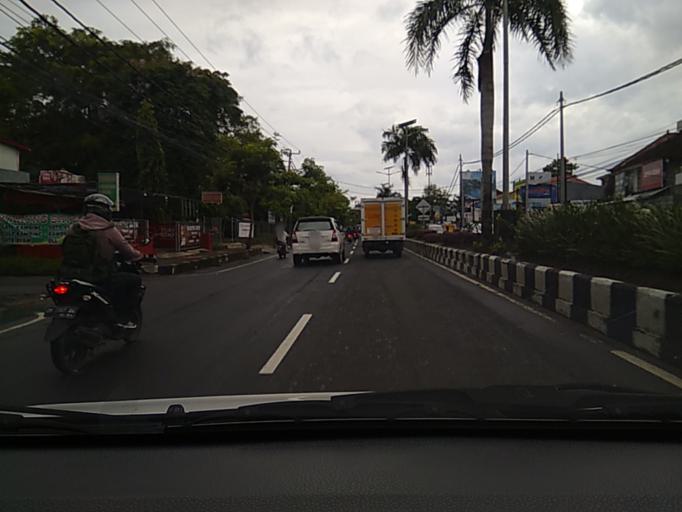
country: ID
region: Bali
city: Bualu
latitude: -8.7849
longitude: 115.1953
